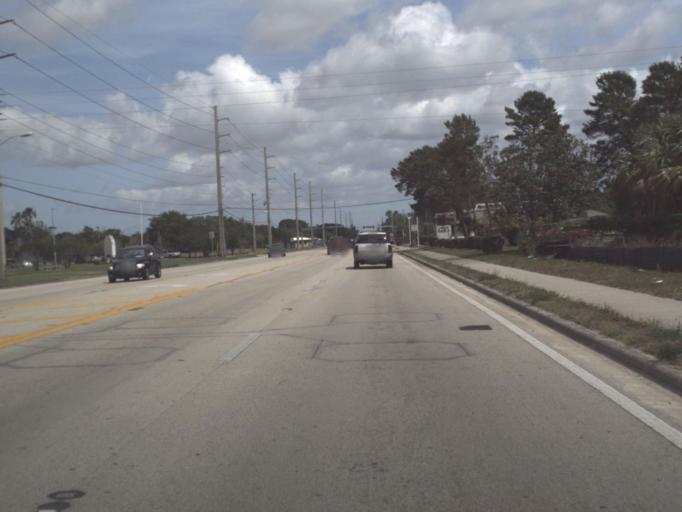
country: US
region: Florida
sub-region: Brevard County
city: Cocoa
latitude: 28.3850
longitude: -80.7550
